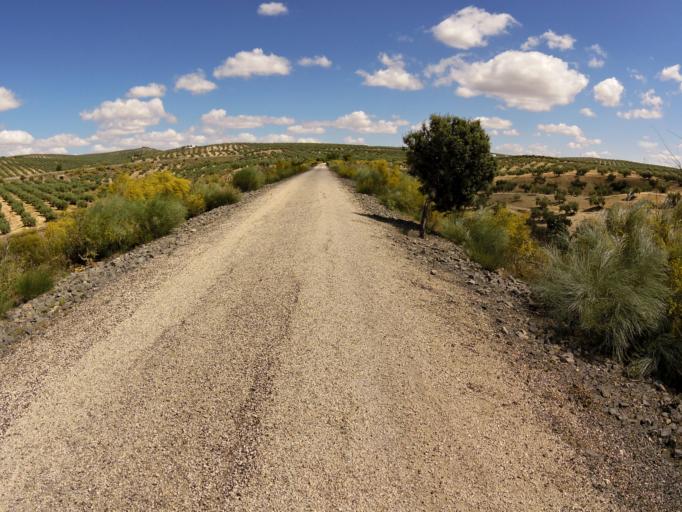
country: ES
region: Andalusia
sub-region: Provincia de Jaen
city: Alcaudete
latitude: 37.6405
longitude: -4.0825
